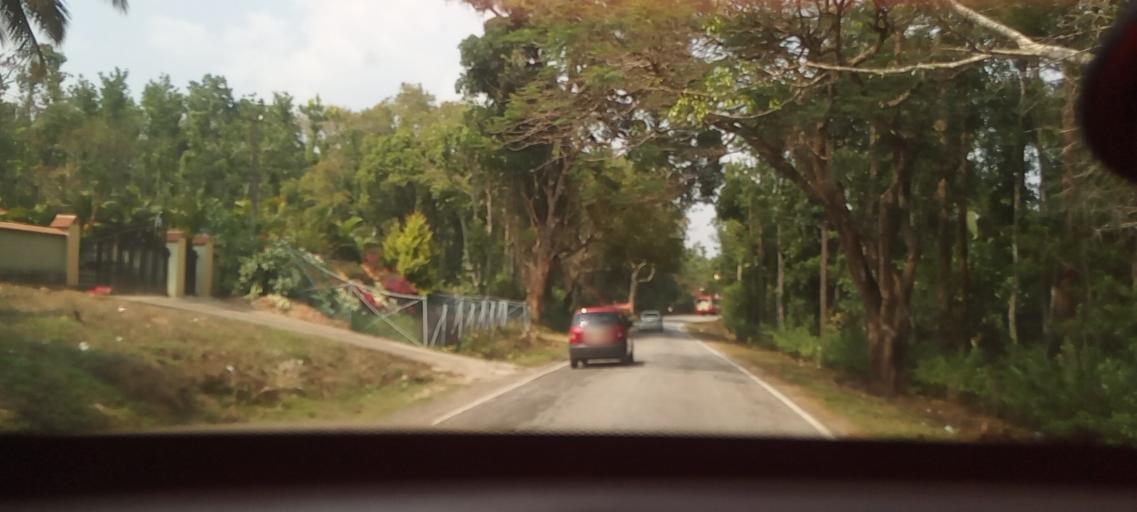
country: IN
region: Karnataka
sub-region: Chikmagalur
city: Chikmagalur
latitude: 13.2598
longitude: 75.6699
